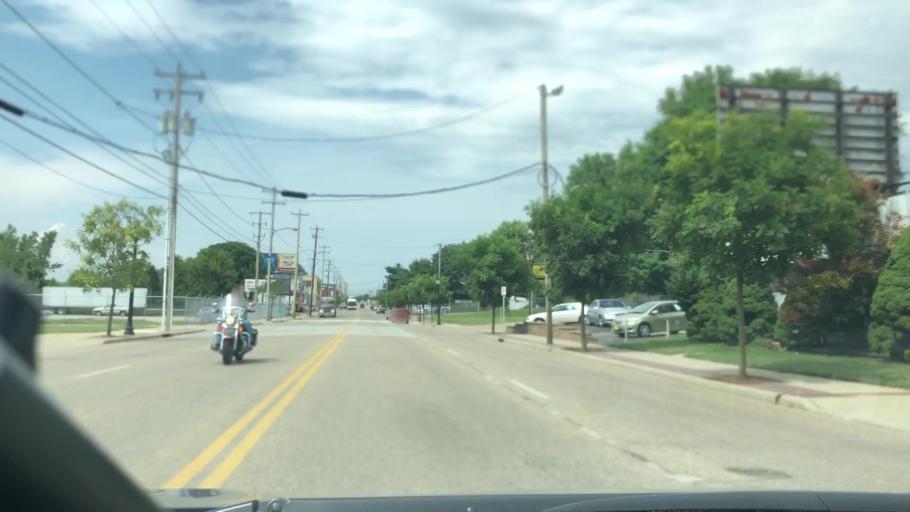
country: US
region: Ohio
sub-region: Summit County
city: Portage Lakes
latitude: 41.0336
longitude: -81.5269
